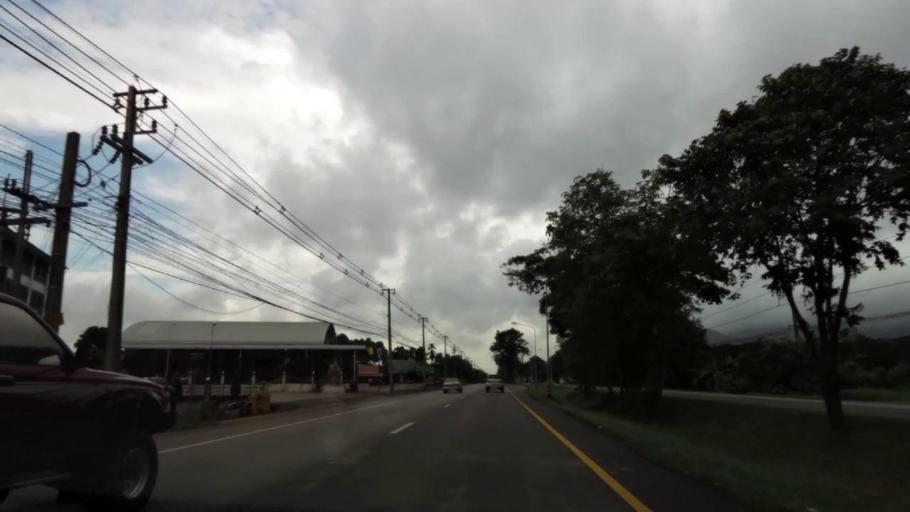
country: TH
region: Chanthaburi
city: Khlung
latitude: 12.4965
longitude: 102.1721
